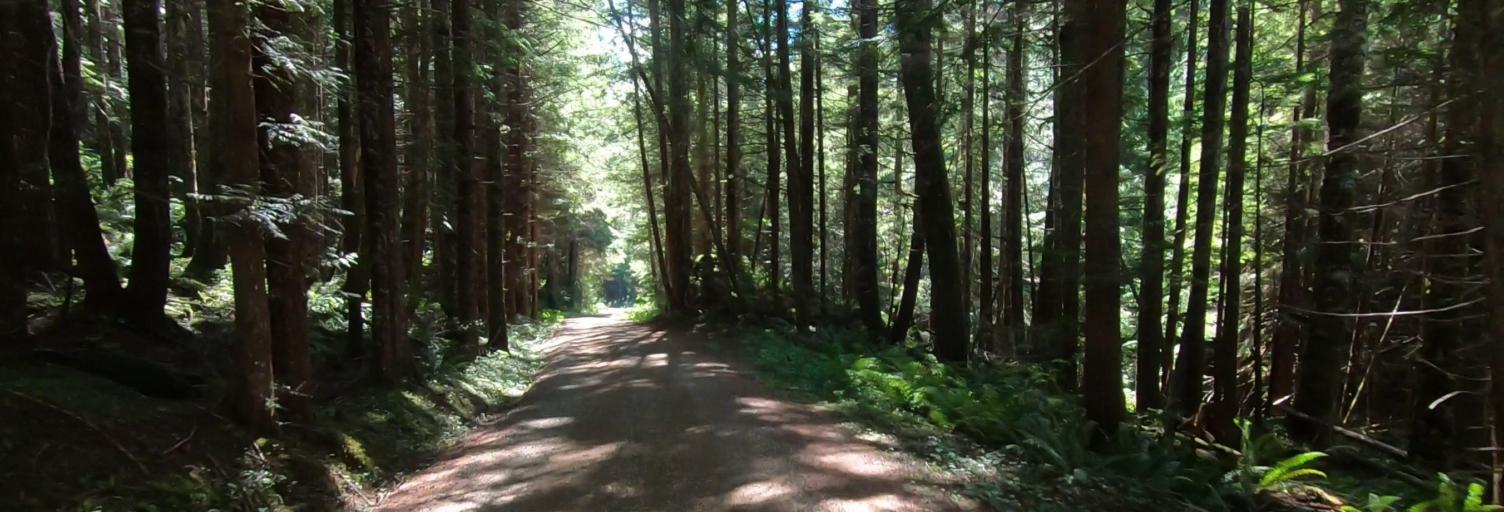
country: CA
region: British Columbia
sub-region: Fraser Valley Regional District
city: Chilliwack
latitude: 48.8656
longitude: -121.7609
